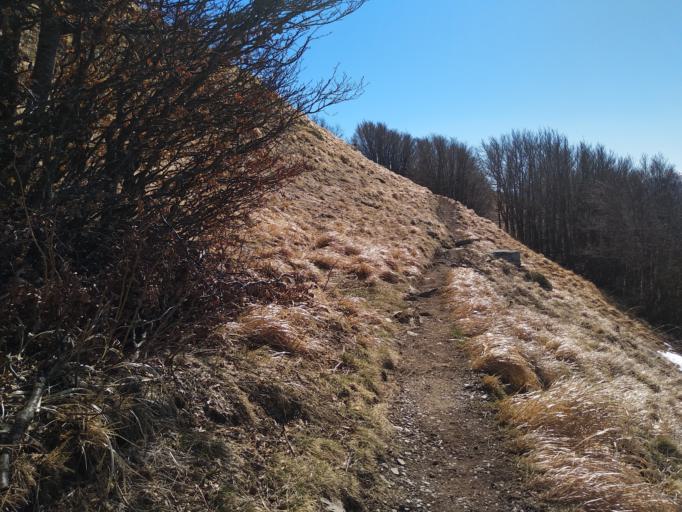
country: IT
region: Emilia-Romagna
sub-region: Provincia di Reggio Emilia
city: Collagna
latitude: 44.3733
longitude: 10.2848
